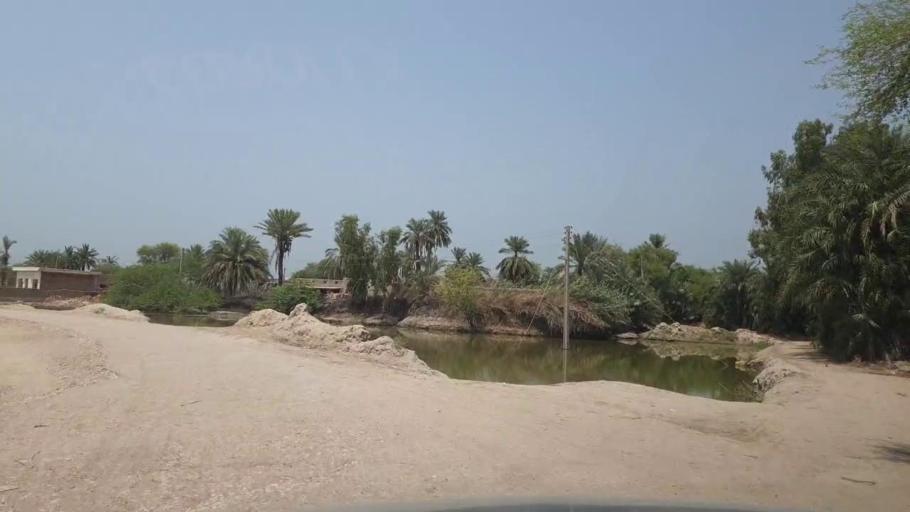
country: PK
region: Sindh
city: Garhi Yasin
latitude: 27.8698
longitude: 68.4554
